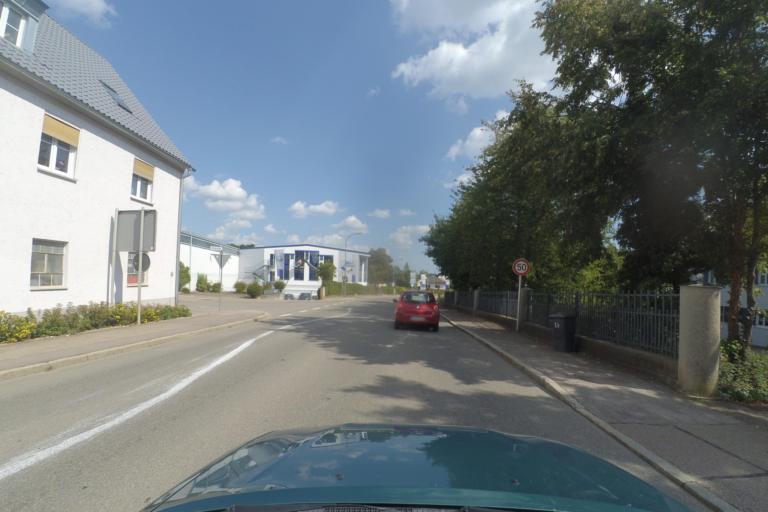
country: DE
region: Bavaria
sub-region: Swabia
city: Oettingen in Bayern
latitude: 48.9572
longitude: 10.5980
